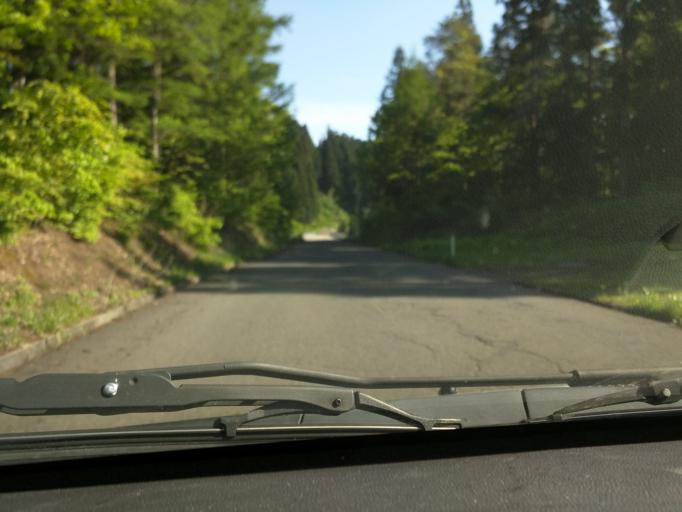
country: JP
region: Fukushima
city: Kitakata
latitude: 37.4805
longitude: 139.6697
